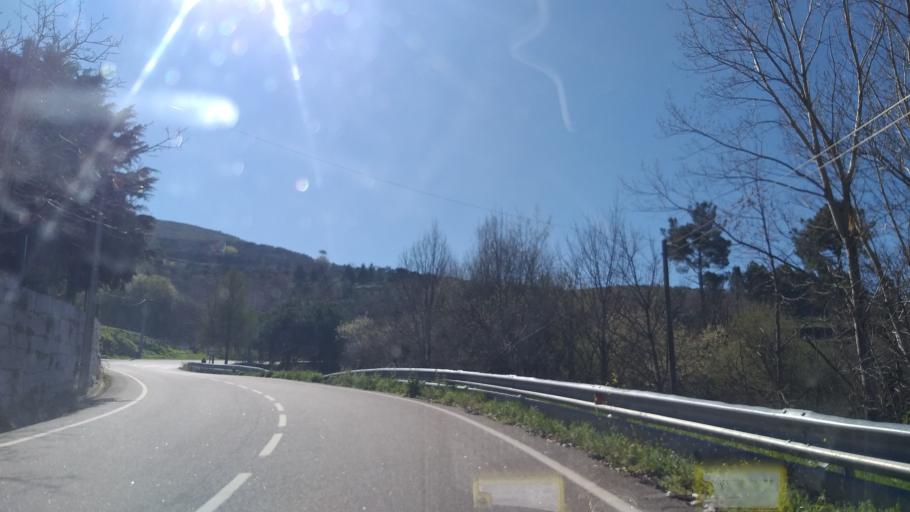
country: PT
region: Guarda
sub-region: Manteigas
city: Manteigas
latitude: 40.5119
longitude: -7.5643
